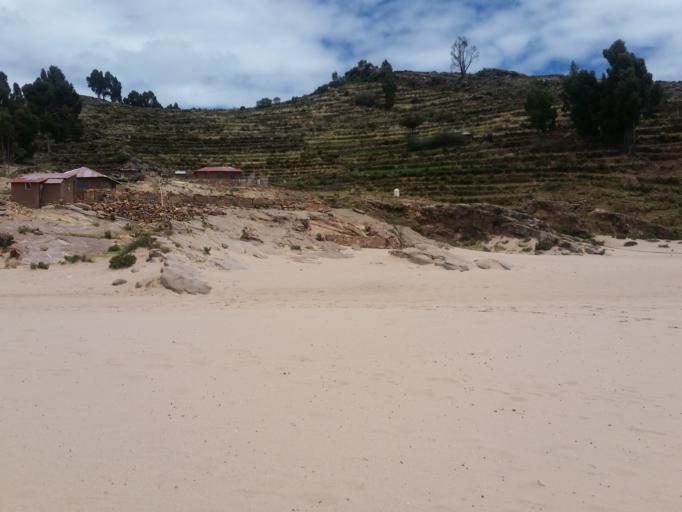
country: PE
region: Puno
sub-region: Provincia de Puno
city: Taquile
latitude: -15.7939
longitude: -69.6804
